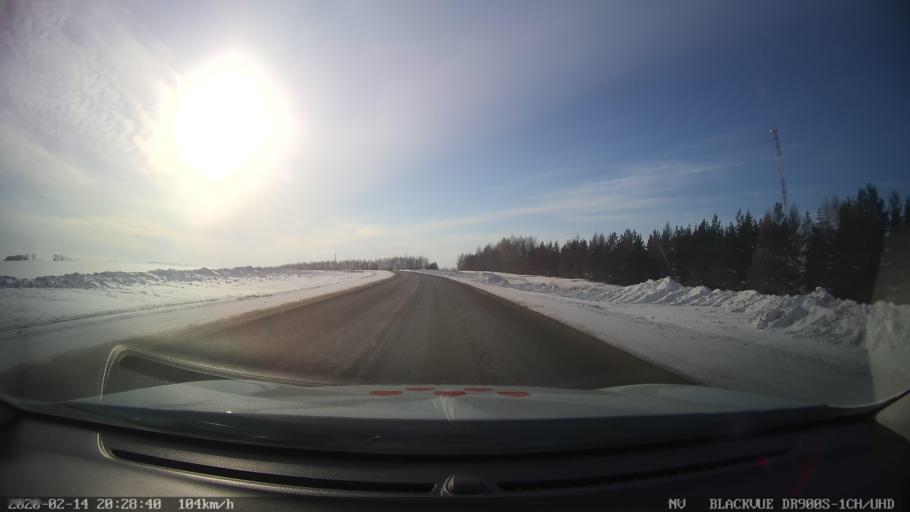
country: RU
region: Tatarstan
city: Stolbishchi
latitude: 55.4599
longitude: 48.9775
